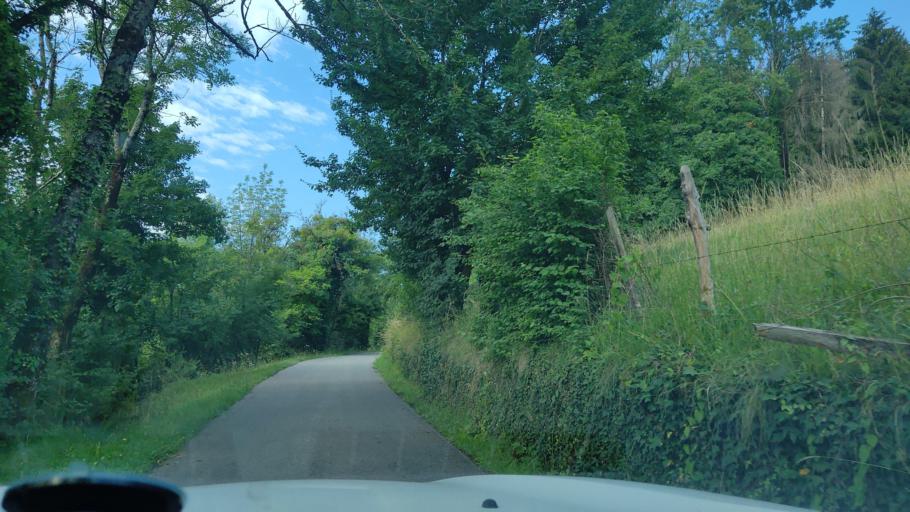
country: FR
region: Rhone-Alpes
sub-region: Departement de la Savoie
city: Coise-Saint-Jean-Pied-Gauthier
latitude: 45.4913
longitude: 6.1390
